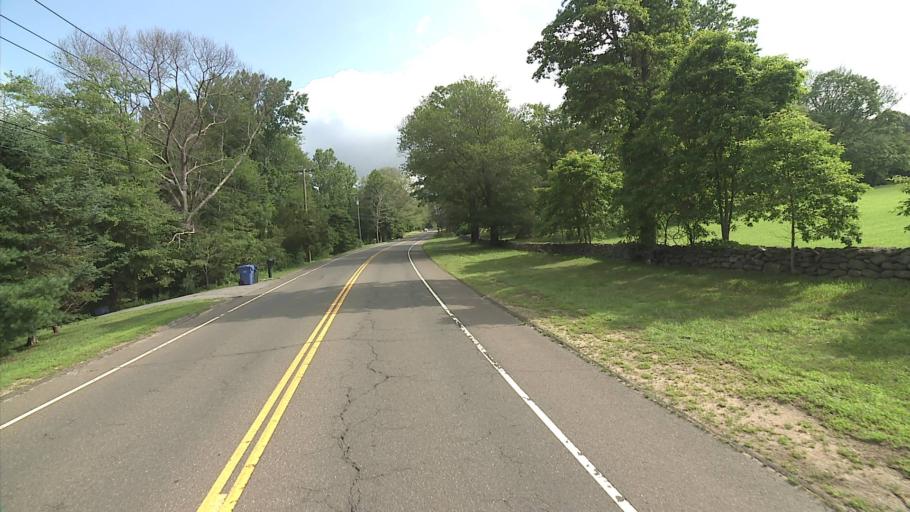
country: US
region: Connecticut
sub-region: Middlesex County
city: Clinton
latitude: 41.3225
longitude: -72.4941
